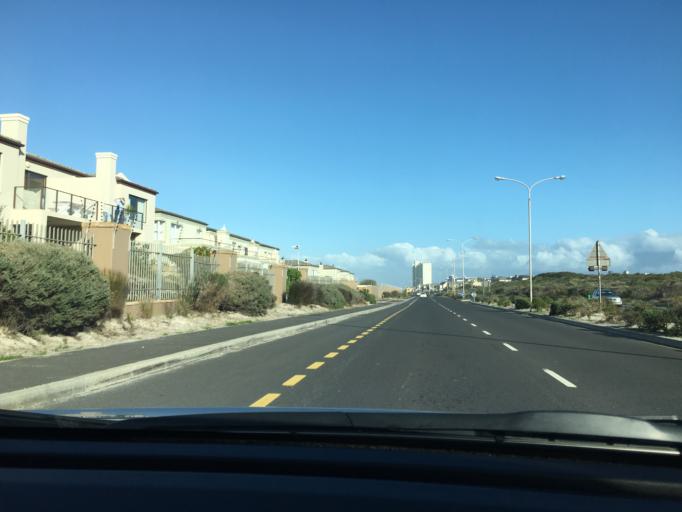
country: ZA
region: Western Cape
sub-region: City of Cape Town
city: Sunset Beach
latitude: -33.7953
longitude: 18.4617
